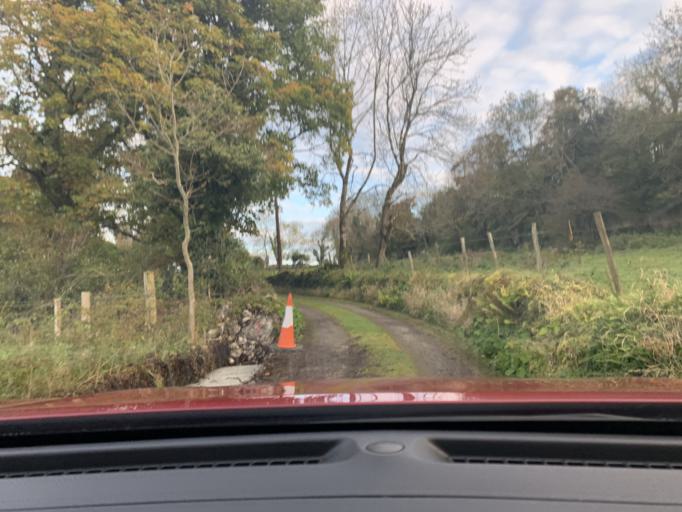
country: IE
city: Ballisodare
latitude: 54.2321
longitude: -8.5029
